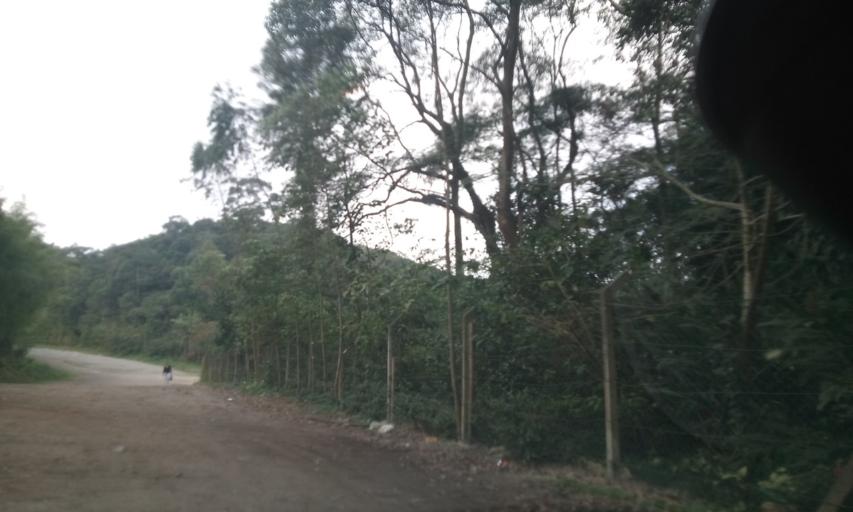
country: BR
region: Sao Paulo
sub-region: Sao Bernardo Do Campo
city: Sao Bernardo do Campo
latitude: -23.7834
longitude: -46.5302
